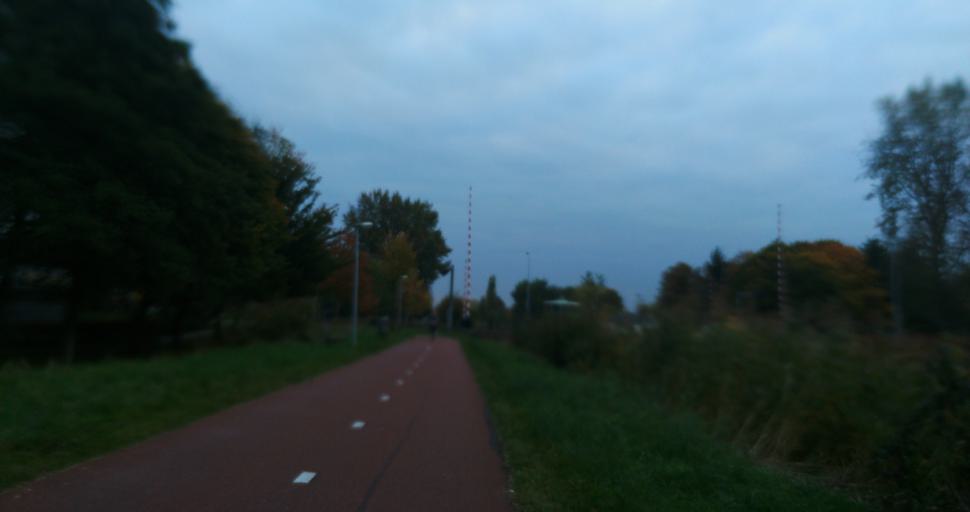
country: NL
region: Groningen
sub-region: Gemeente Groningen
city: Groningen
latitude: 53.2281
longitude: 6.5352
